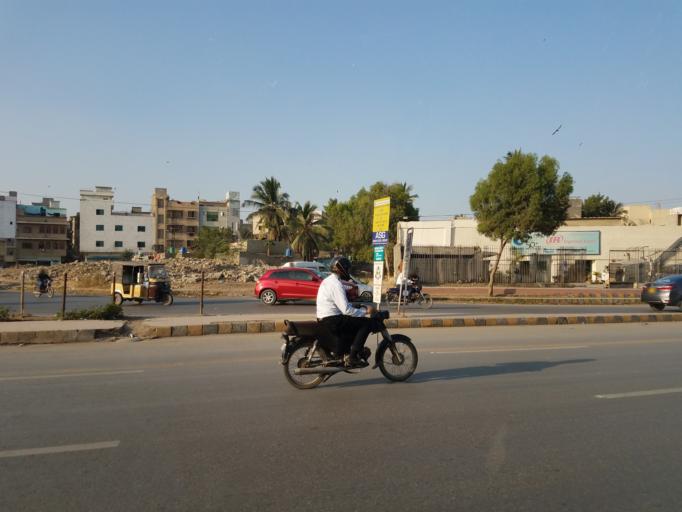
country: PK
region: Sindh
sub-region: Karachi District
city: Karachi
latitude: 24.8590
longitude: 67.0515
